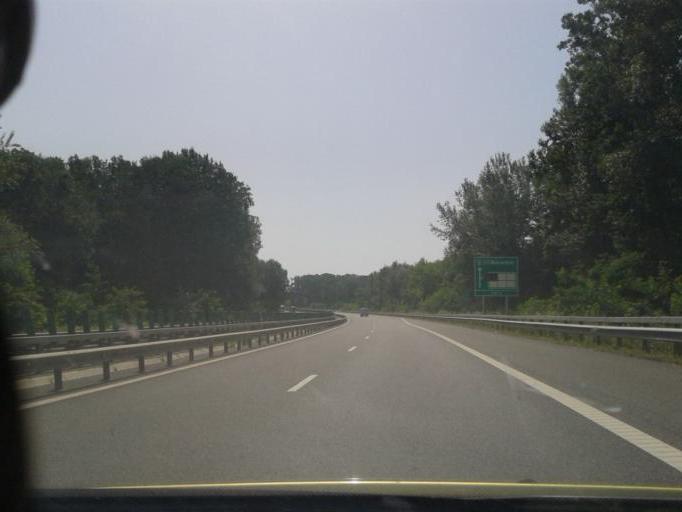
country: RO
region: Prahova
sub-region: Comuna Rafov
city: Rafov
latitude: 44.8622
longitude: 26.1502
